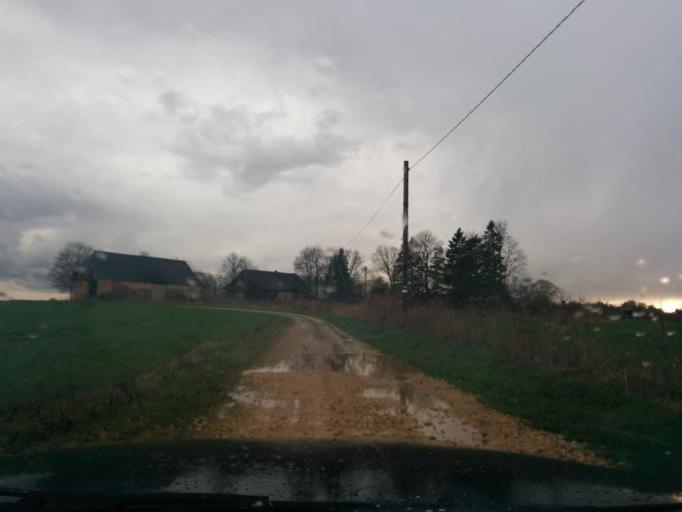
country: LV
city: Tervete
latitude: 56.3670
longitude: 23.5065
